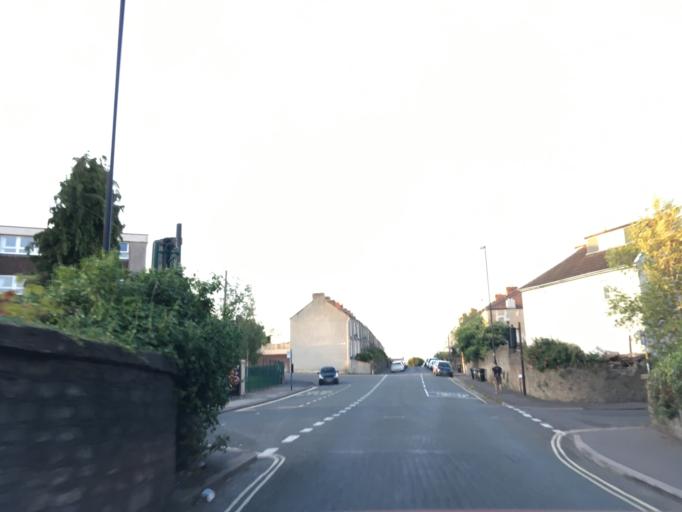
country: GB
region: England
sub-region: South Gloucestershire
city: Mangotsfield
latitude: 51.4790
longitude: -2.5166
